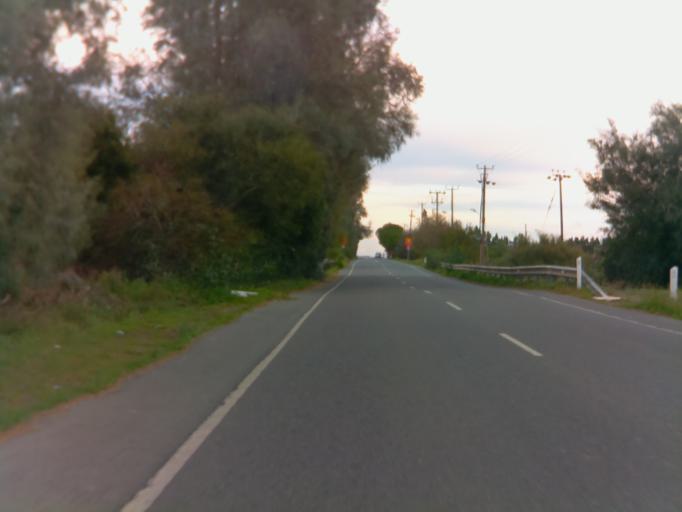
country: CY
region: Pafos
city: Pegeia
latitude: 34.8643
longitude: 32.3697
